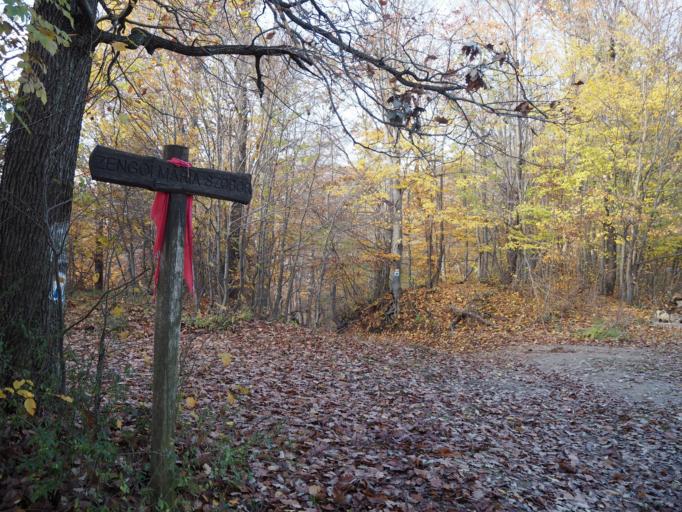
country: HU
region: Baranya
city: Hosszuheteny
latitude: 46.1894
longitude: 18.3748
